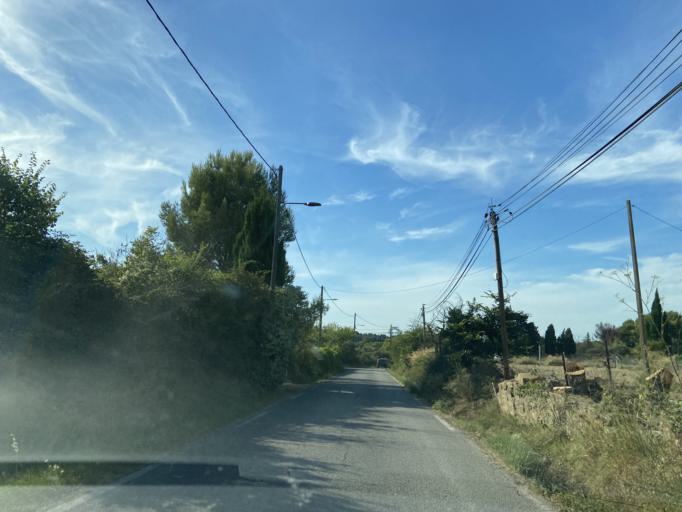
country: FR
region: Provence-Alpes-Cote d'Azur
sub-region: Departement des Bouches-du-Rhone
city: Saint-Chamas
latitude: 43.5665
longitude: 5.0201
